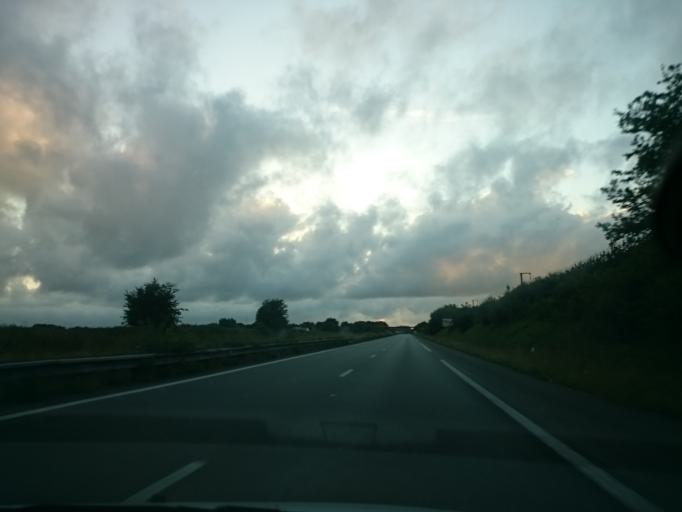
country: FR
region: Brittany
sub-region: Departement du Finistere
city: Redene
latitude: 47.8381
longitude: -3.4916
